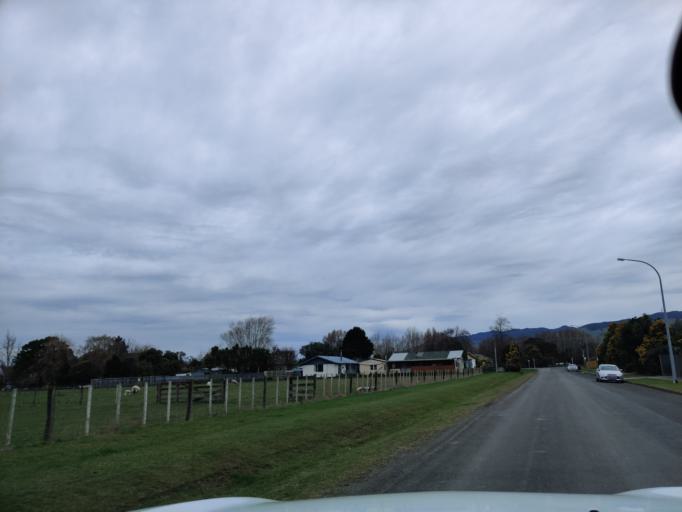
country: NZ
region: Manawatu-Wanganui
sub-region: Palmerston North City
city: Palmerston North
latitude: -40.2848
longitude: 175.7489
